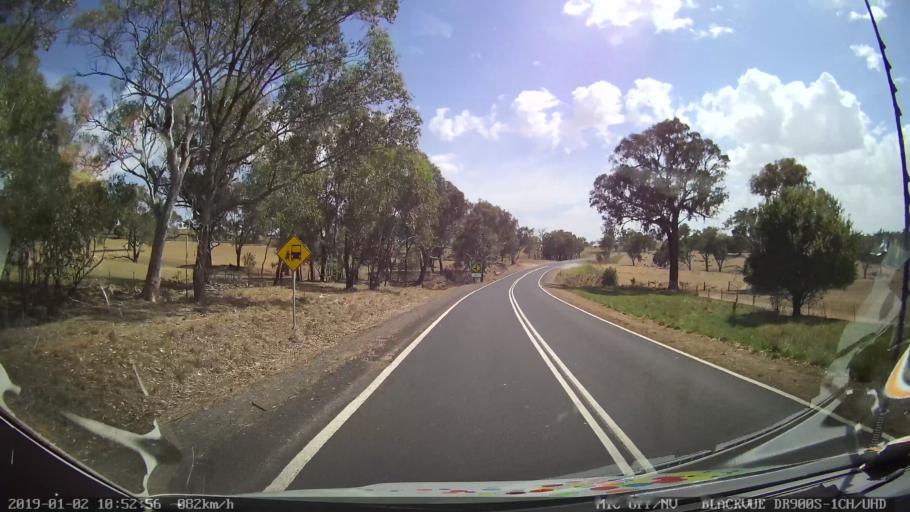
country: AU
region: New South Wales
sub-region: Cootamundra
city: Cootamundra
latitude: -34.6831
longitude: 148.2714
